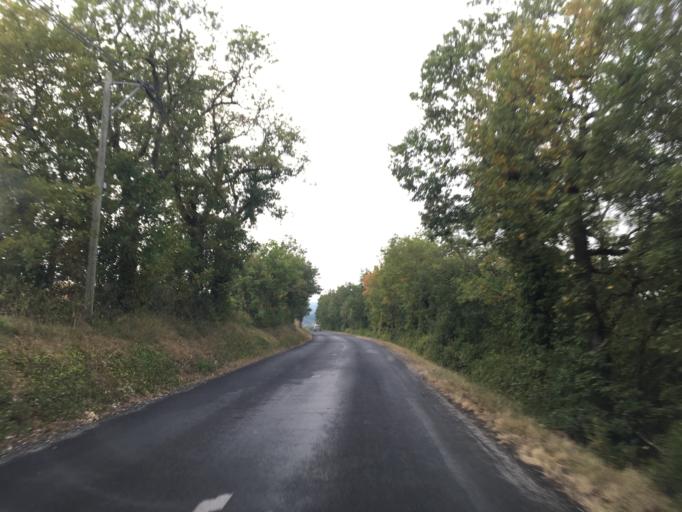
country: FR
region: Midi-Pyrenees
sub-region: Departement du Lot
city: Souillac
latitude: 44.8327
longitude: 1.5642
